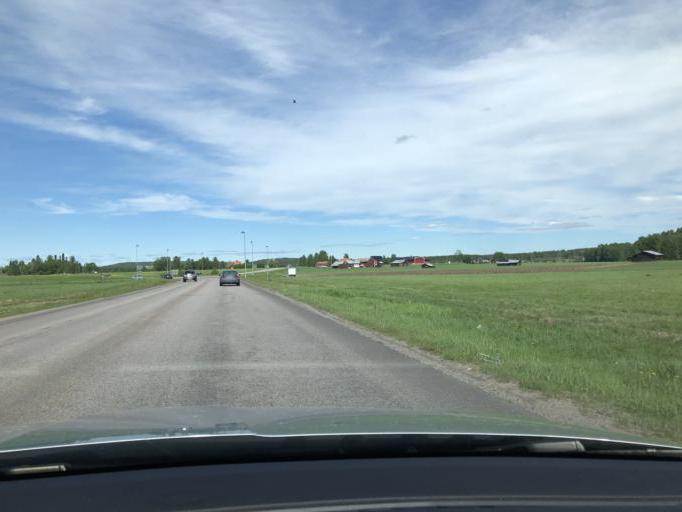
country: SE
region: Norrbotten
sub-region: Pitea Kommun
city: Bergsviken
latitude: 65.3505
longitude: 21.4032
